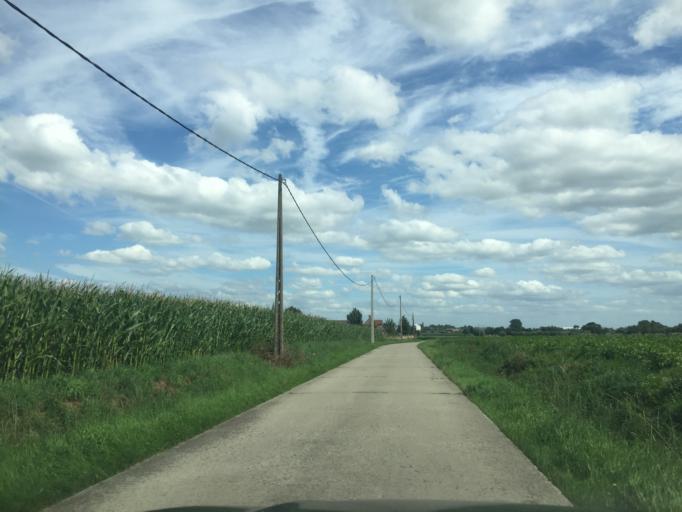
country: BE
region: Flanders
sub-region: Provincie West-Vlaanderen
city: Staden
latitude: 50.9889
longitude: 3.0373
